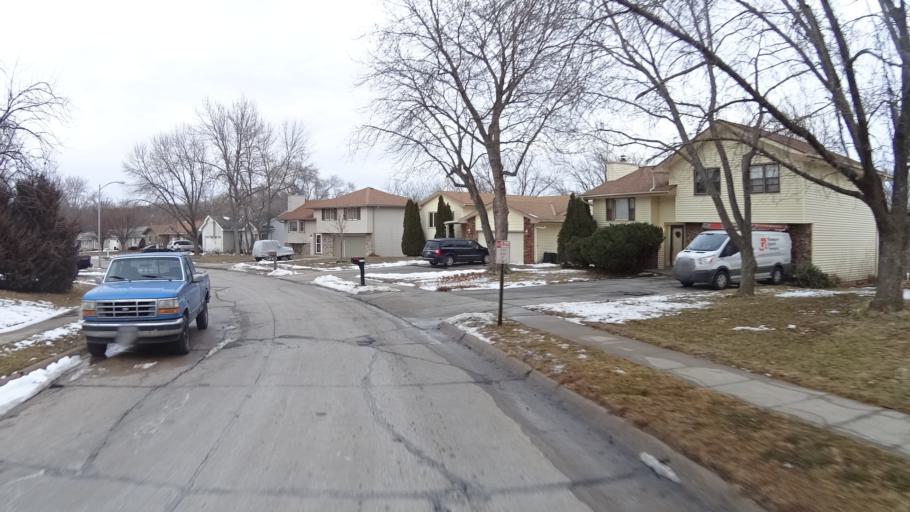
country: US
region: Nebraska
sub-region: Sarpy County
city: Offutt Air Force Base
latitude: 41.1626
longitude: -95.9417
